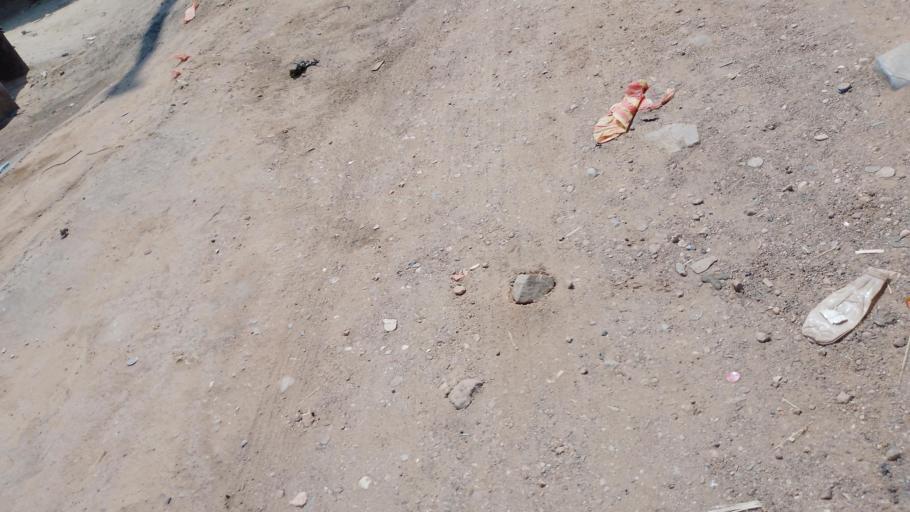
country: ZM
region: Lusaka
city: Lusaka
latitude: -15.3972
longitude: 28.3689
